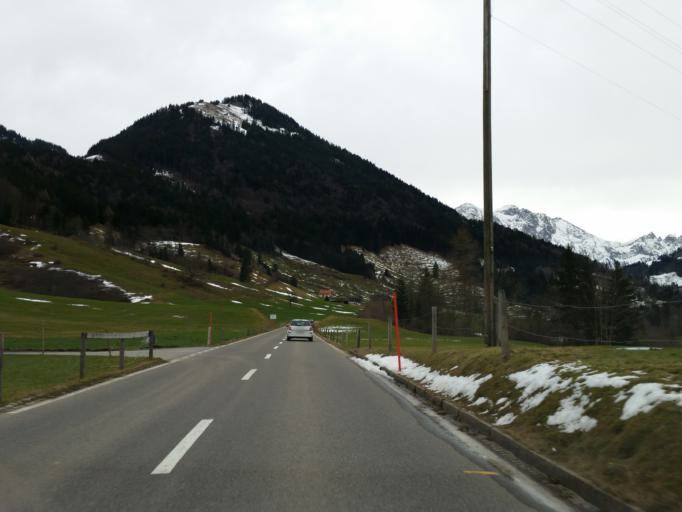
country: CH
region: Appenzell Ausserrhoden
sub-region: Bezirk Hinterland
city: Urnasch
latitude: 47.2951
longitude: 9.2733
